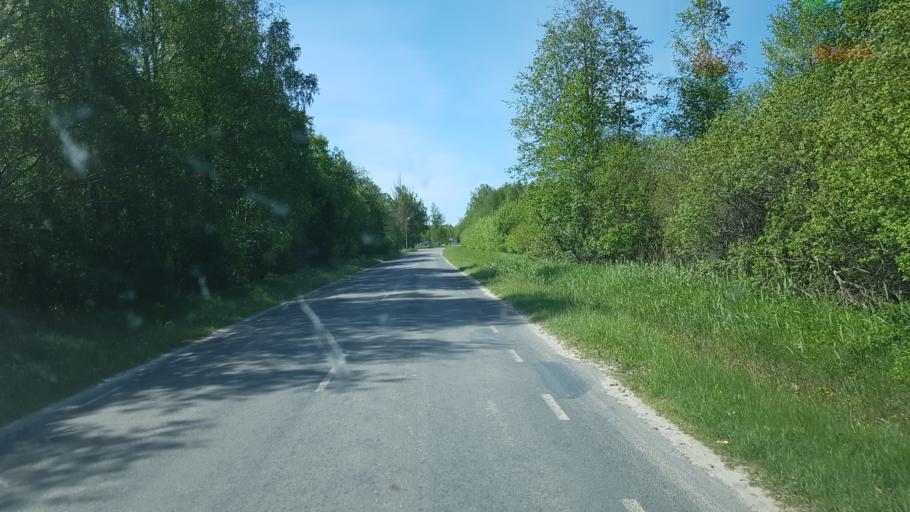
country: EE
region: Saare
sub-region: Kuressaare linn
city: Kuressaare
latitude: 58.2747
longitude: 22.4987
